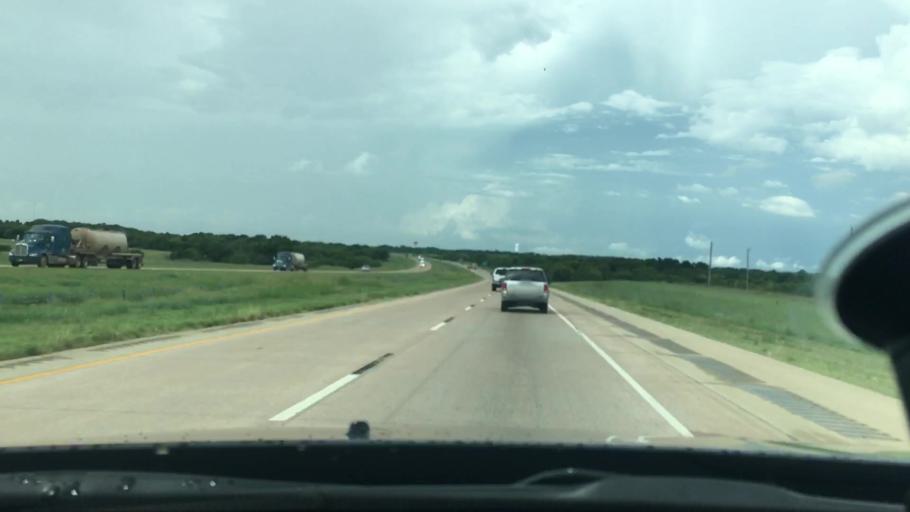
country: US
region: Oklahoma
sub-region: Garvin County
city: Pauls Valley
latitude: 34.6836
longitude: -97.2287
